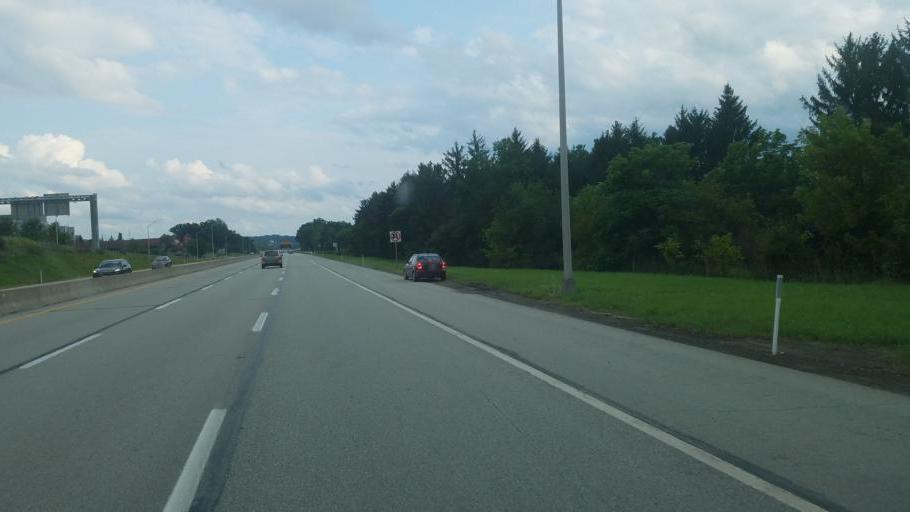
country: US
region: Pennsylvania
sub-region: Butler County
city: Cranberry Township
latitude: 40.6782
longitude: -80.1039
